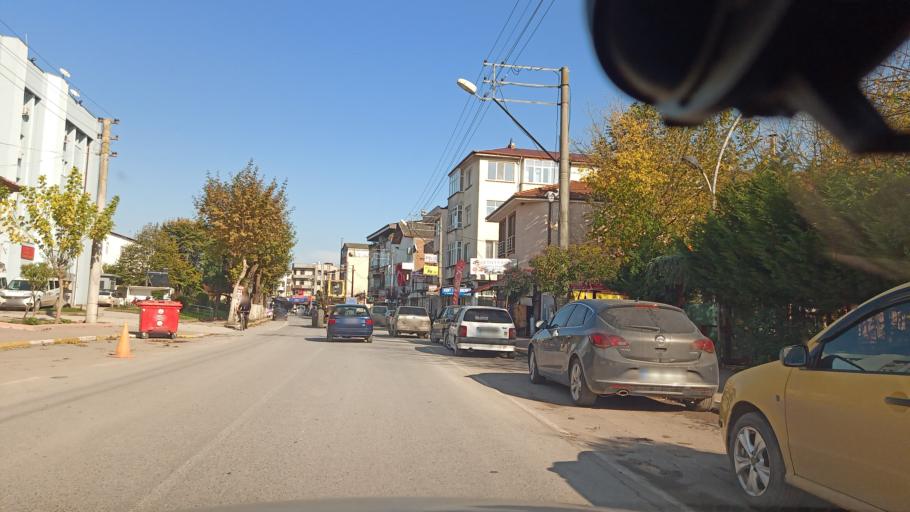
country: TR
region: Sakarya
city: Sogutlu
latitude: 40.9045
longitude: 30.4727
